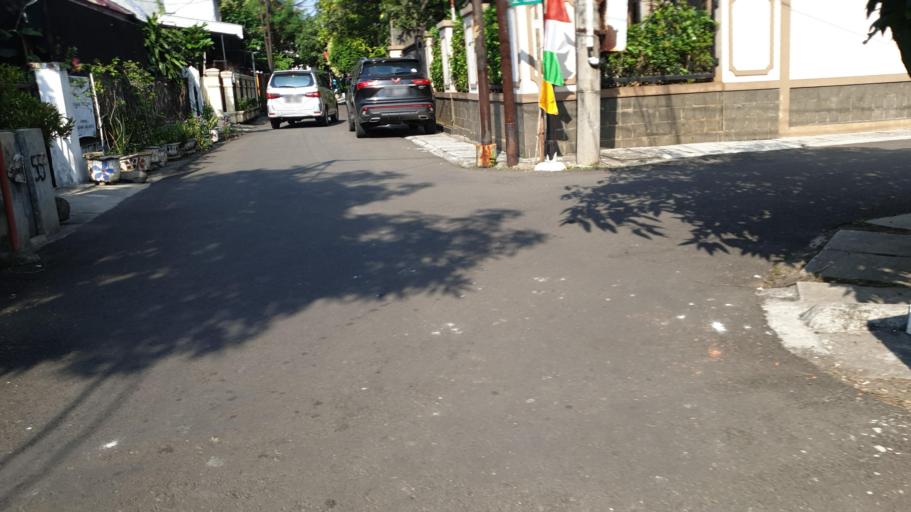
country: ID
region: Jakarta Raya
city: Jakarta
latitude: -6.3000
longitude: 106.8393
